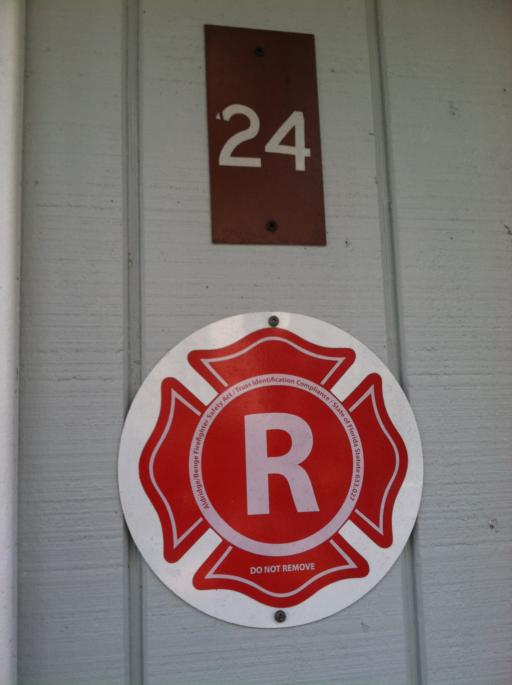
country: US
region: Florida
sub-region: Gulf County
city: Port Saint Joe
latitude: 29.7799
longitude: -85.4071
